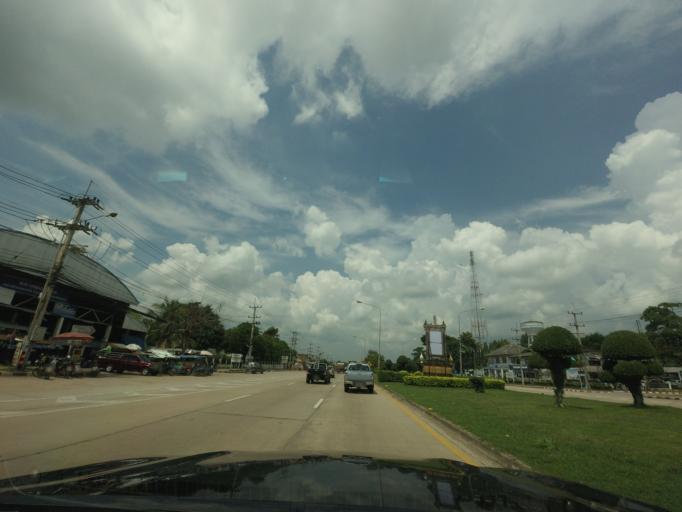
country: TH
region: Khon Kaen
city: Nong Ruea
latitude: 16.4917
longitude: 102.4334
